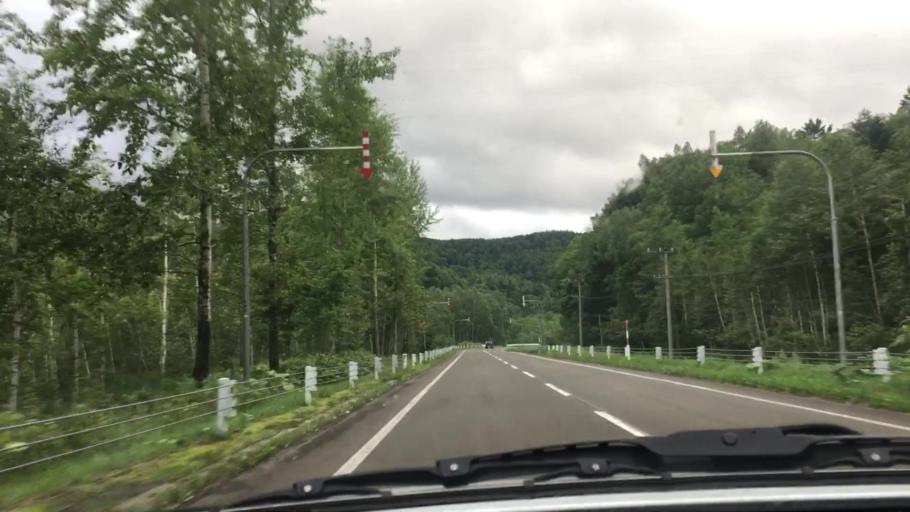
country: JP
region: Hokkaido
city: Shimo-furano
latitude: 43.0526
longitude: 142.5330
